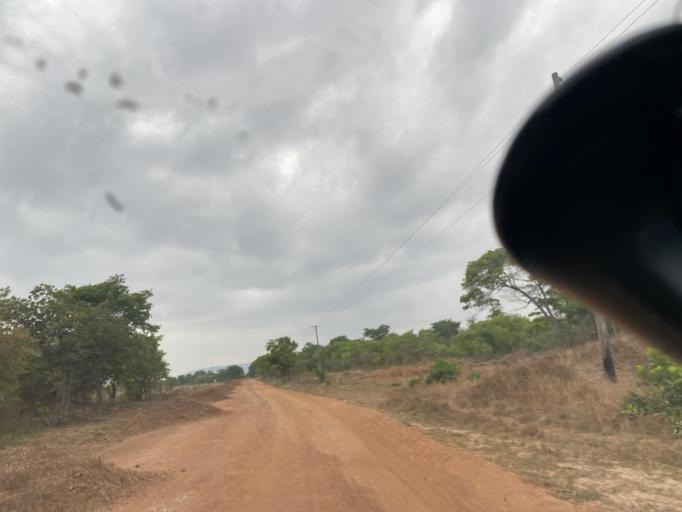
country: ZM
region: Lusaka
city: Chongwe
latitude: -15.2297
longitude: 28.7263
